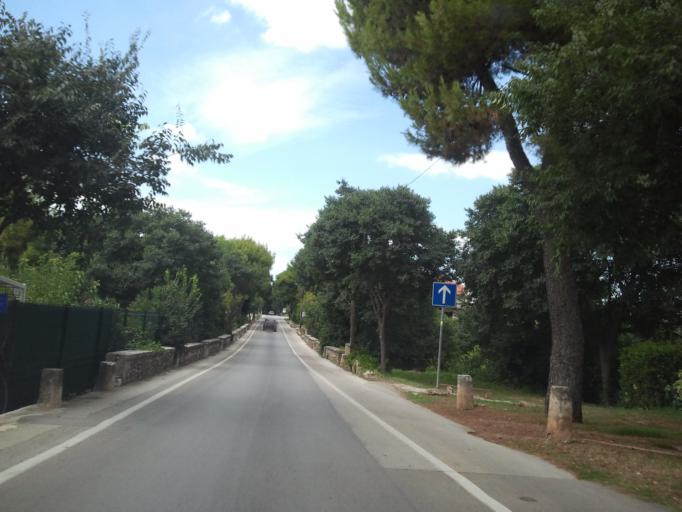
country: HR
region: Zadarska
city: Zadar
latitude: 44.1289
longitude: 15.2234
